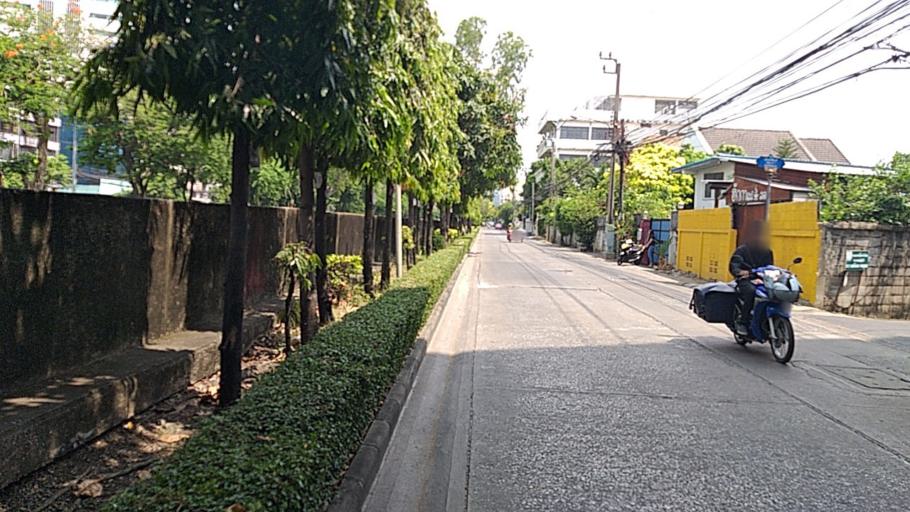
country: TH
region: Bangkok
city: Bang Sue
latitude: 13.8133
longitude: 100.5354
